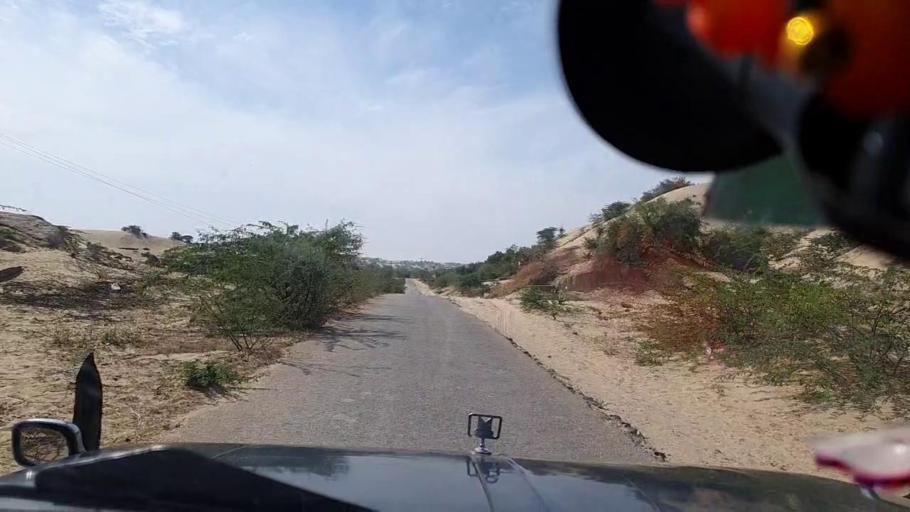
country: PK
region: Sindh
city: Diplo
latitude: 24.4548
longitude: 69.5793
